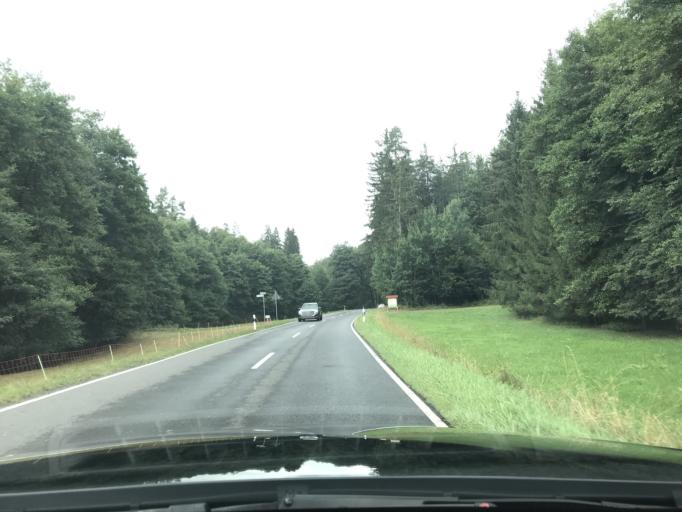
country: DE
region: Bavaria
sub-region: Regierungsbezirk Unterfranken
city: Breitbrunn
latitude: 50.0151
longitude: 10.6771
